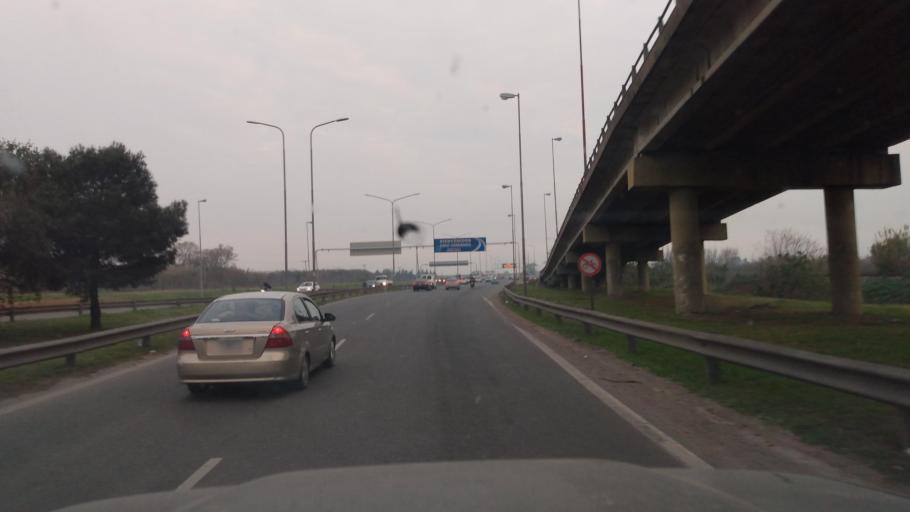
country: AR
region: Buenos Aires
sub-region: Partido de Tigre
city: Tigre
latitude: -34.4887
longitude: -58.5967
